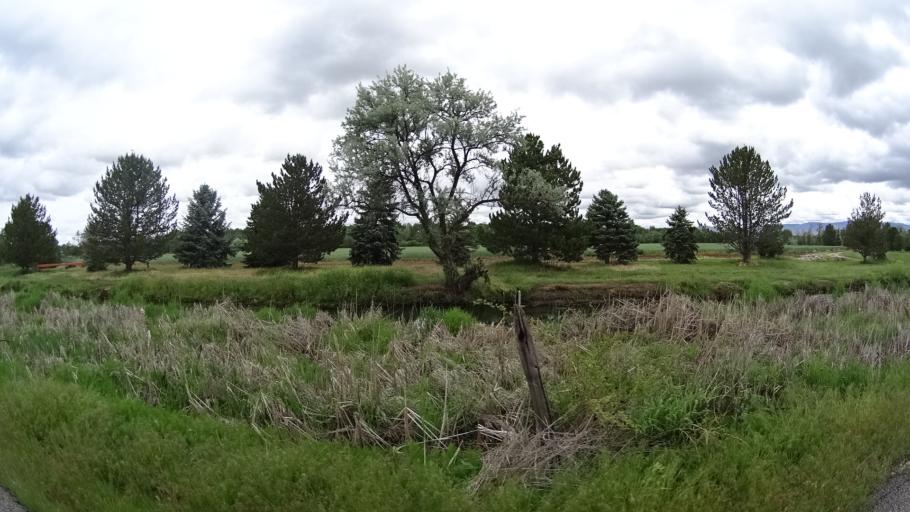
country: US
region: Idaho
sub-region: Ada County
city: Eagle
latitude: 43.6841
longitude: -116.3815
